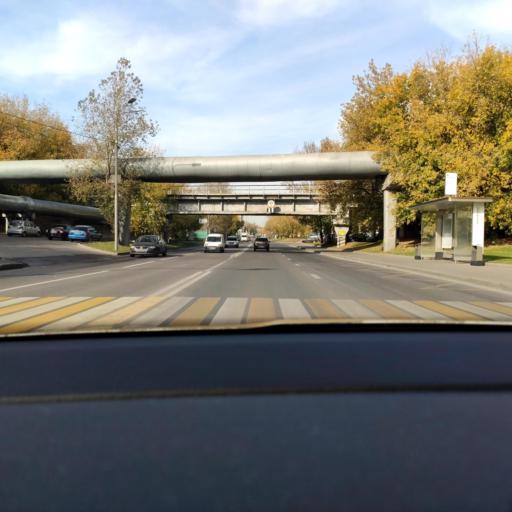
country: RU
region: Moscow
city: Metrogorodok
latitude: 55.8180
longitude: 37.7681
